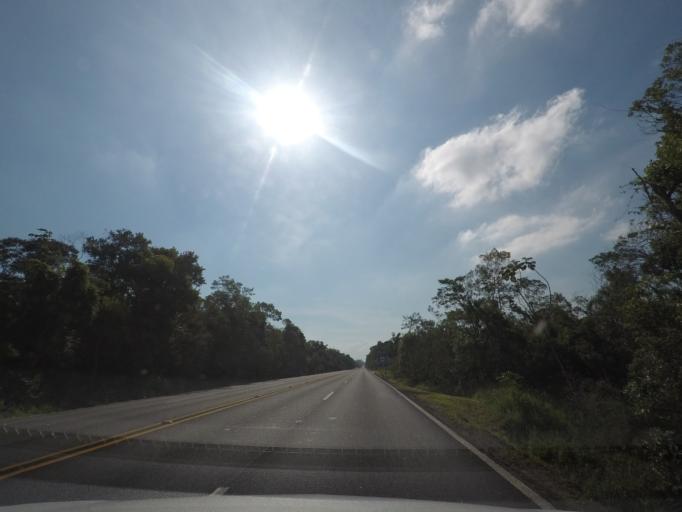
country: BR
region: Parana
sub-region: Pontal Do Parana
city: Pontal do Parana
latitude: -25.6250
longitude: -48.5977
